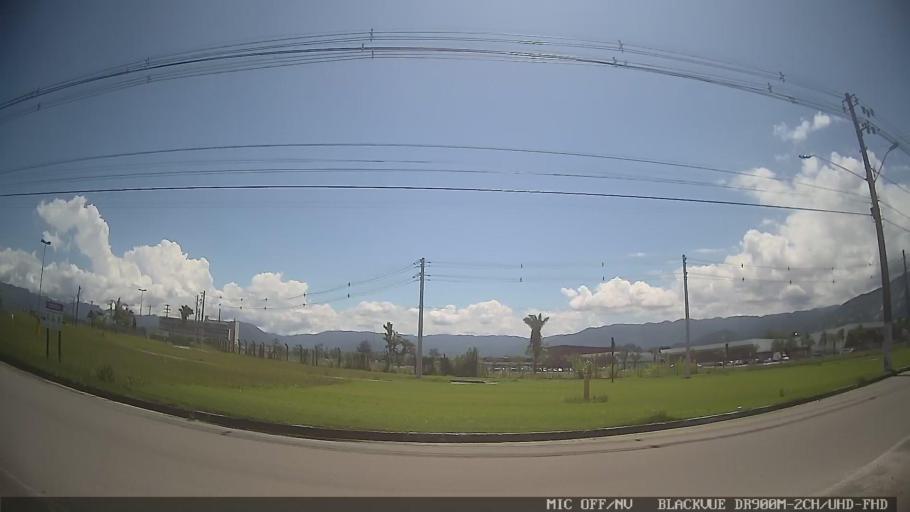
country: BR
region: Sao Paulo
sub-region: Caraguatatuba
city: Caraguatatuba
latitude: -23.6561
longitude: -45.4341
